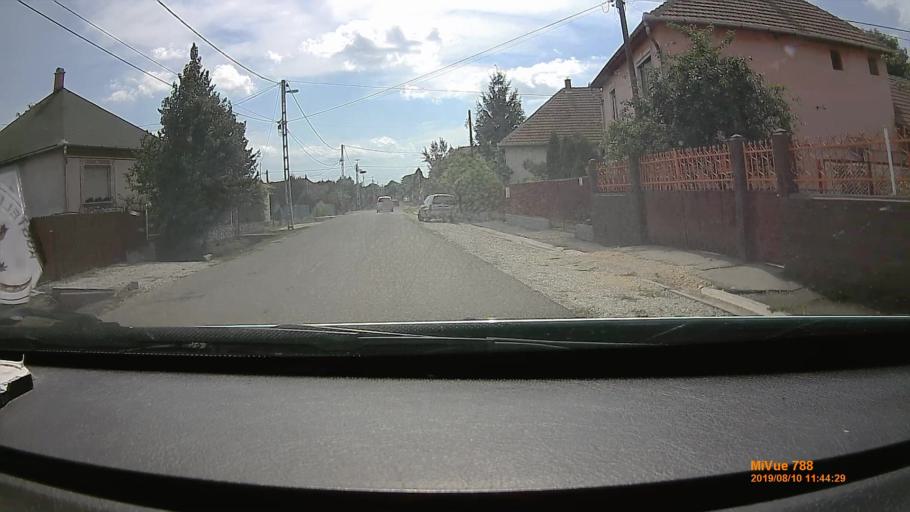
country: HU
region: Borsod-Abauj-Zemplen
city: Szentistvan
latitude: 47.7213
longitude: 20.6216
